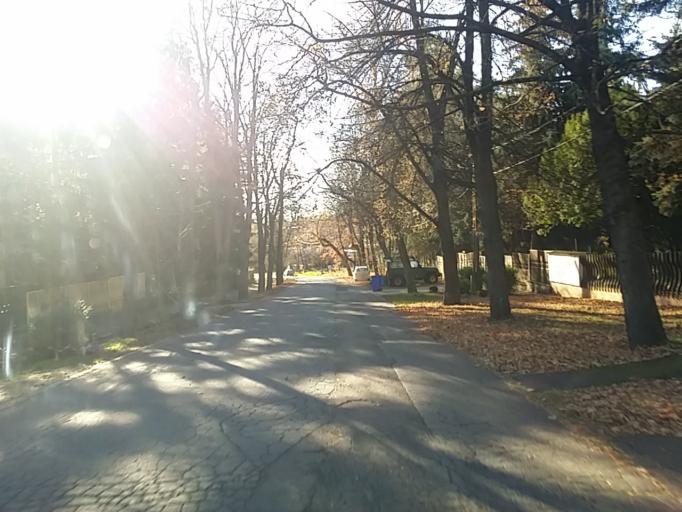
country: HU
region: Heves
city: Gyongyossolymos
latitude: 47.8318
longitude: 19.9647
